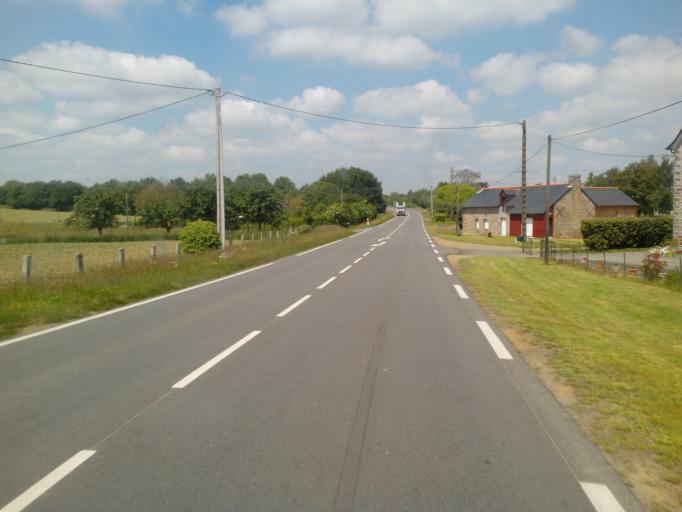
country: FR
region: Brittany
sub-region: Departement d'Ille-et-Vilaine
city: Saint-Germain-en-Cogles
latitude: 48.3951
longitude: -1.2936
